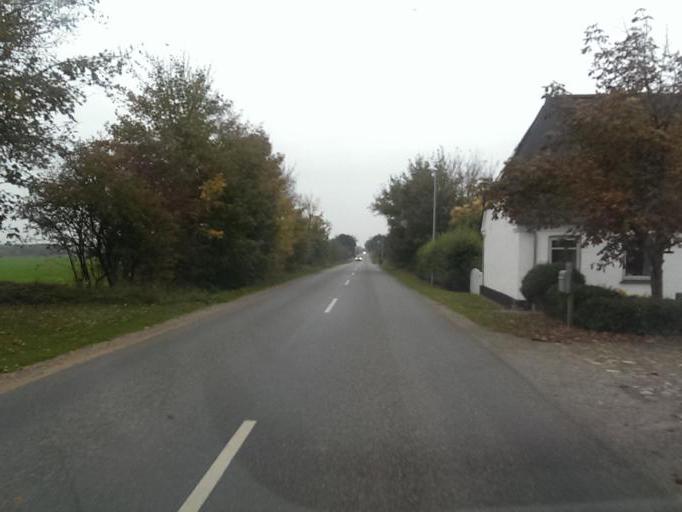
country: DK
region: South Denmark
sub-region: Esbjerg Kommune
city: Tjaereborg
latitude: 55.4817
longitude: 8.5556
